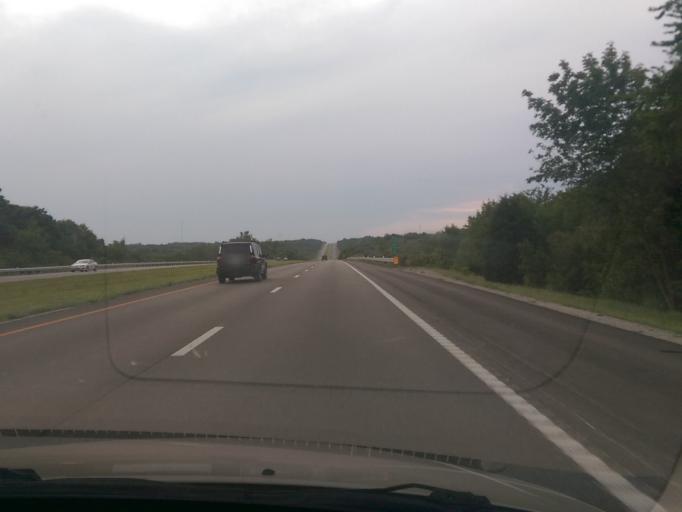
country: US
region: Missouri
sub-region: Andrew County
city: Savannah
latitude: 39.9305
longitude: -94.9234
